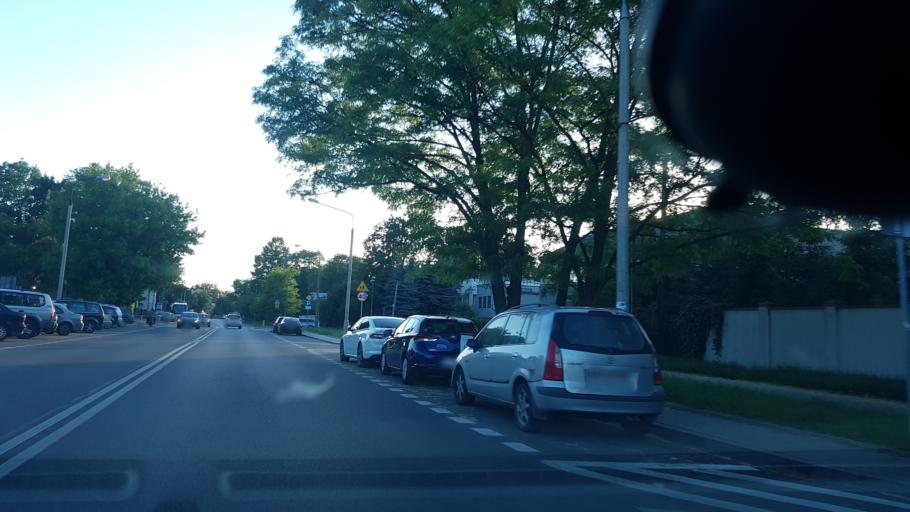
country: PL
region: Masovian Voivodeship
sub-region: Warszawa
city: Wawer
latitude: 52.2073
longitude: 21.1900
